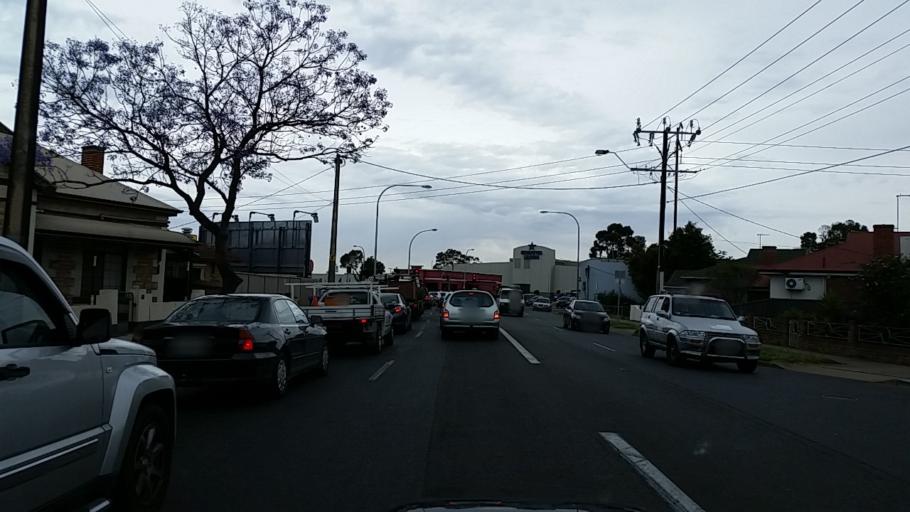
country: AU
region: South Australia
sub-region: Charles Sturt
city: Woodville
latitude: -34.8776
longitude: 138.5506
